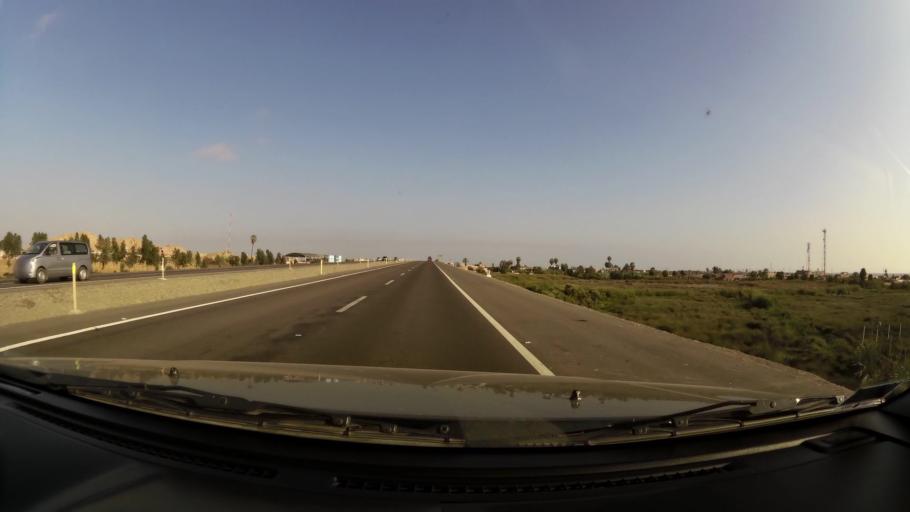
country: PE
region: Ica
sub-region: Provincia de Chincha
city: Chincha Baja
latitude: -13.4548
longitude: -76.1793
